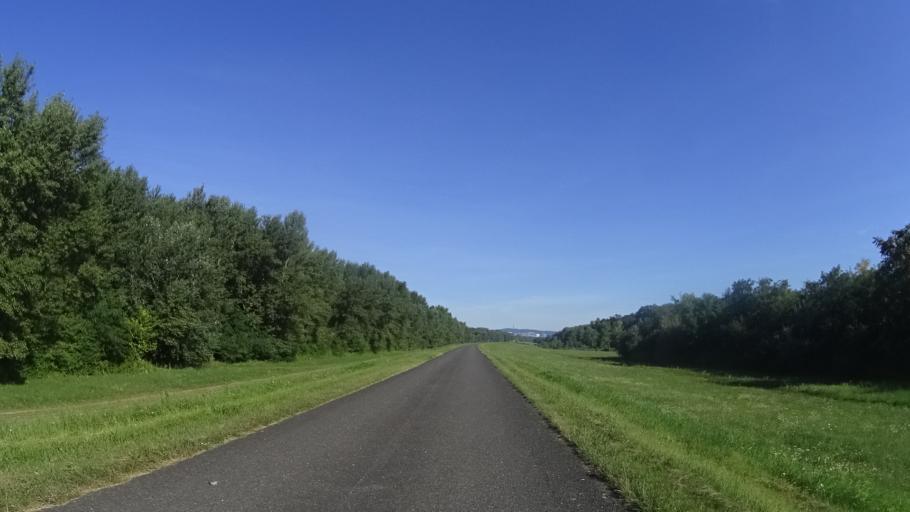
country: AT
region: Burgenland
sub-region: Politischer Bezirk Neusiedl am See
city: Deutsch Jahrndorf
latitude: 48.0773
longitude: 17.1620
